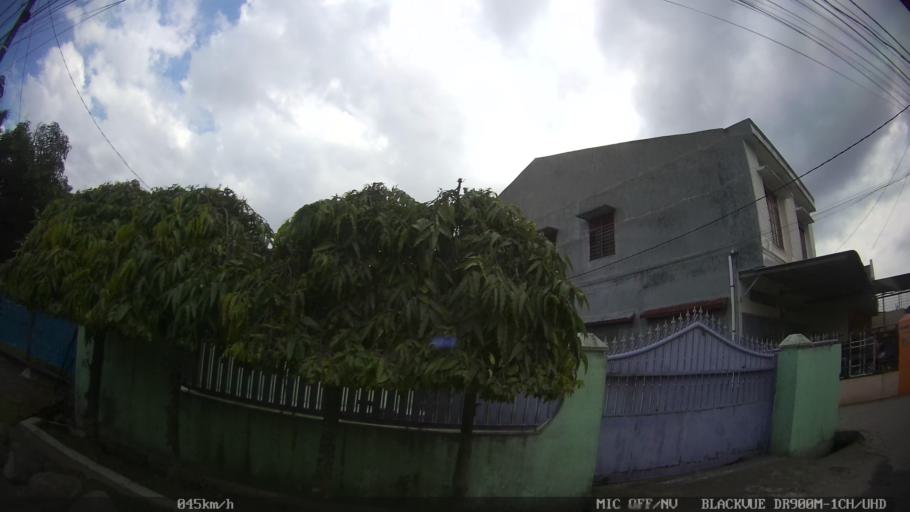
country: ID
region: North Sumatra
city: Sunggal
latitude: 3.6166
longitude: 98.6250
